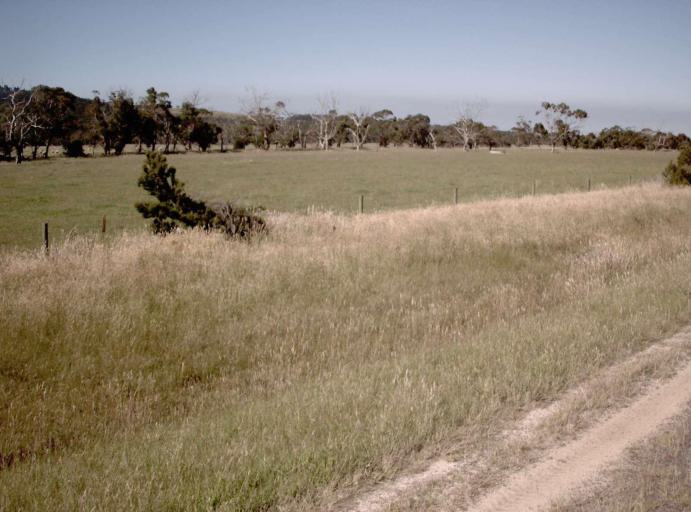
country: AU
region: Victoria
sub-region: Latrobe
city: Morwell
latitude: -38.6328
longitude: 146.5510
